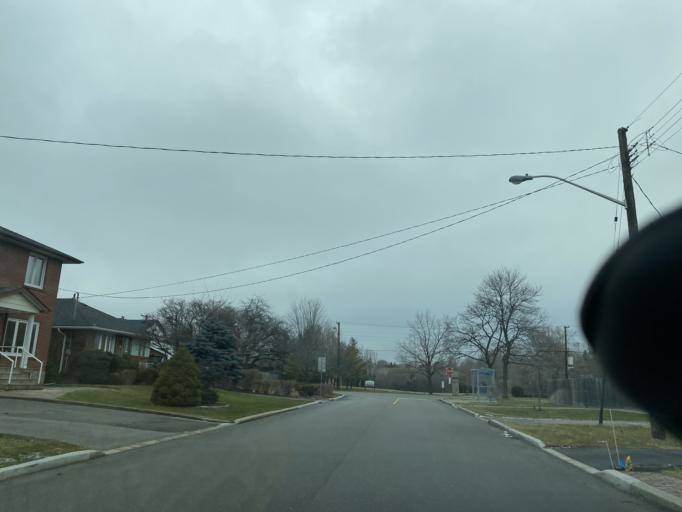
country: CA
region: Ontario
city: Scarborough
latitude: 43.7648
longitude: -79.3104
